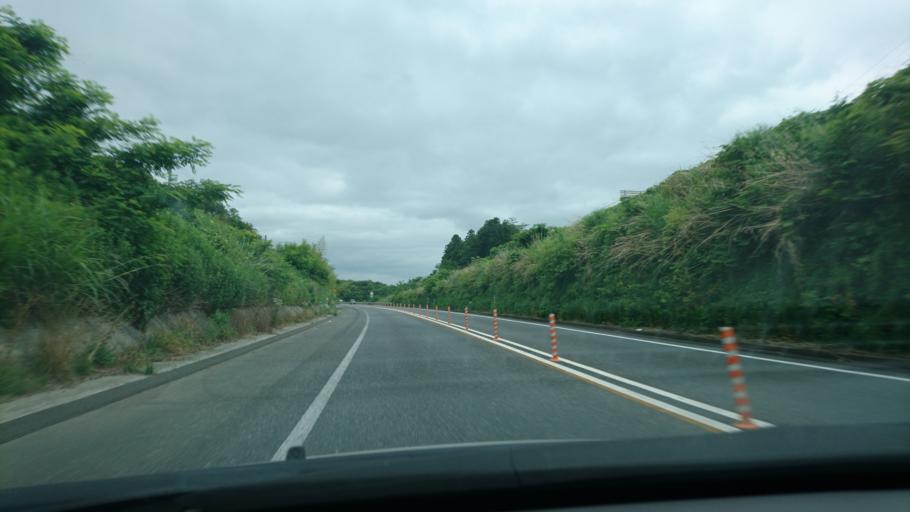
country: JP
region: Miyagi
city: Kogota
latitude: 38.7277
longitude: 141.0635
